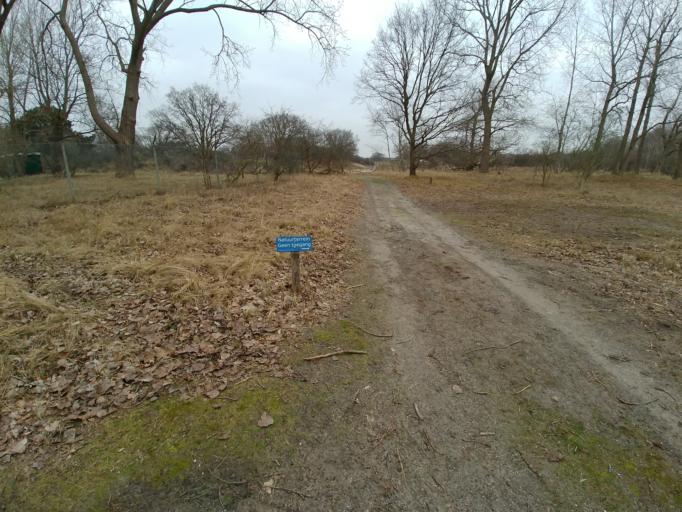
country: NL
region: South Holland
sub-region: Gemeente Den Haag
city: The Hague
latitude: 52.1131
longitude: 4.3280
